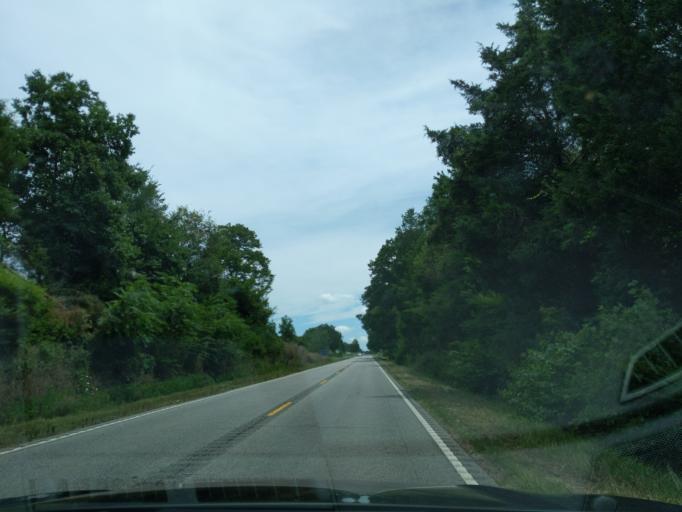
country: US
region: North Carolina
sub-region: Rowan County
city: Rockwell
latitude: 35.4580
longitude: -80.3312
